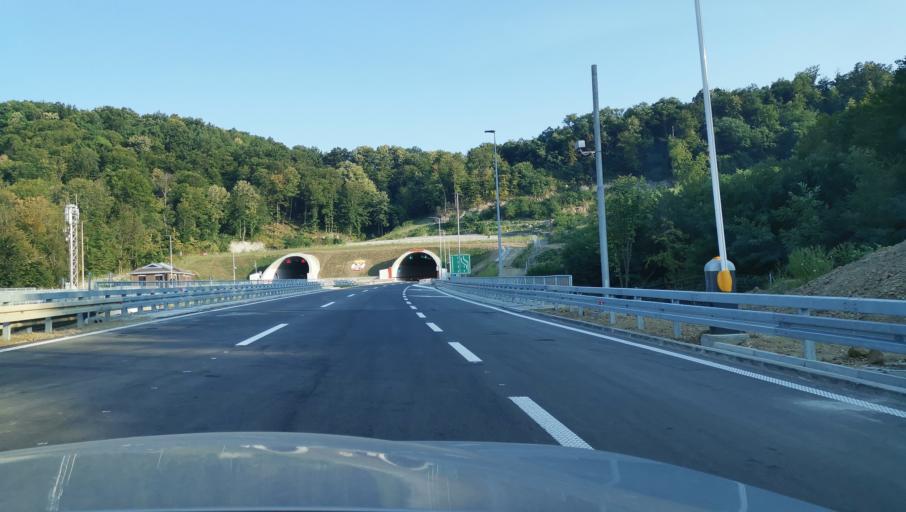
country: RS
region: Central Serbia
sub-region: Kolubarski Okrug
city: Ljig
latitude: 44.2127
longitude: 20.2620
